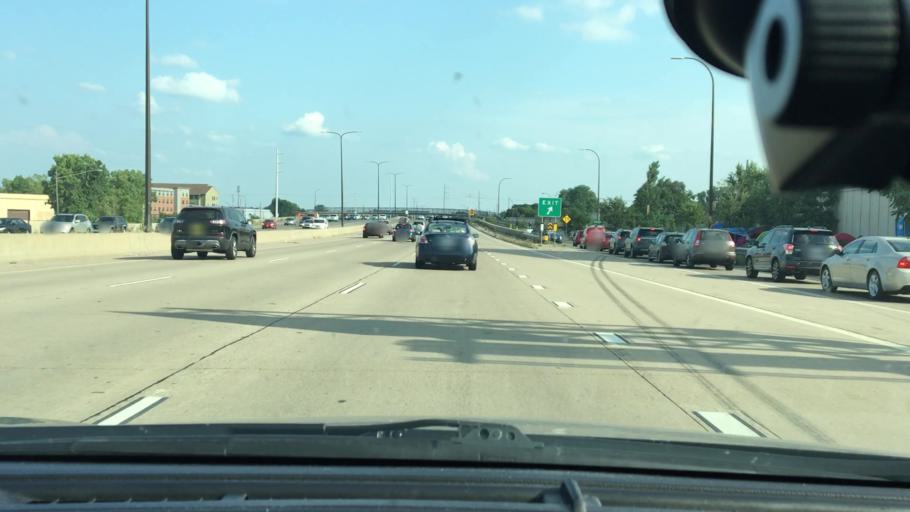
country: US
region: Minnesota
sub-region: Hennepin County
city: Minneapolis
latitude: 44.9619
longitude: -93.2489
